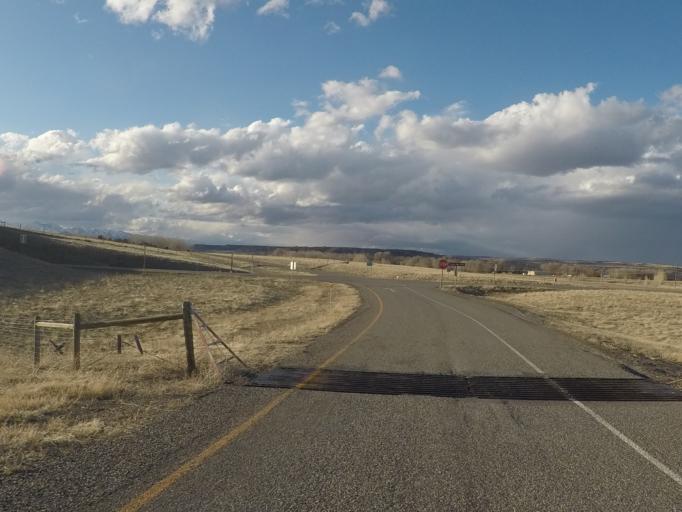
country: US
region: Montana
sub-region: Sweet Grass County
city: Big Timber
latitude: 45.7689
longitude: -109.7923
